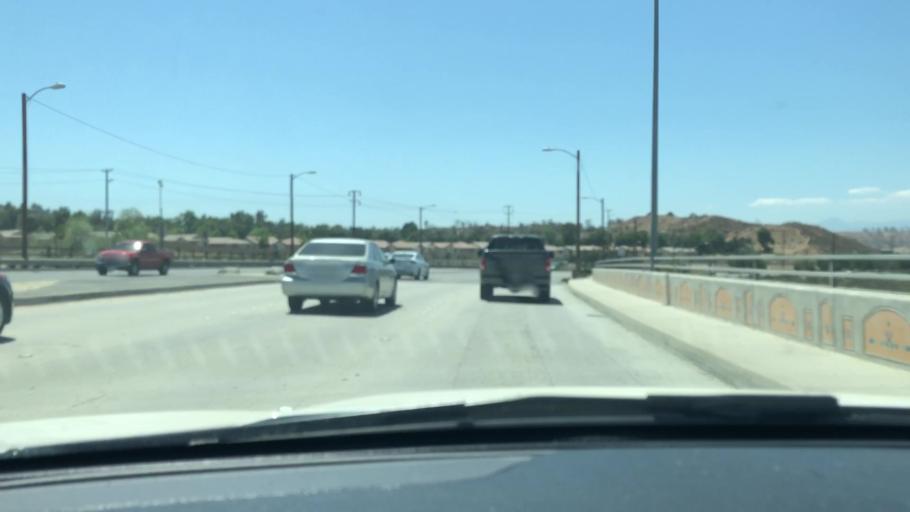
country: US
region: California
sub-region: Los Angeles County
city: Santa Clarita
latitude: 34.4158
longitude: -118.4777
